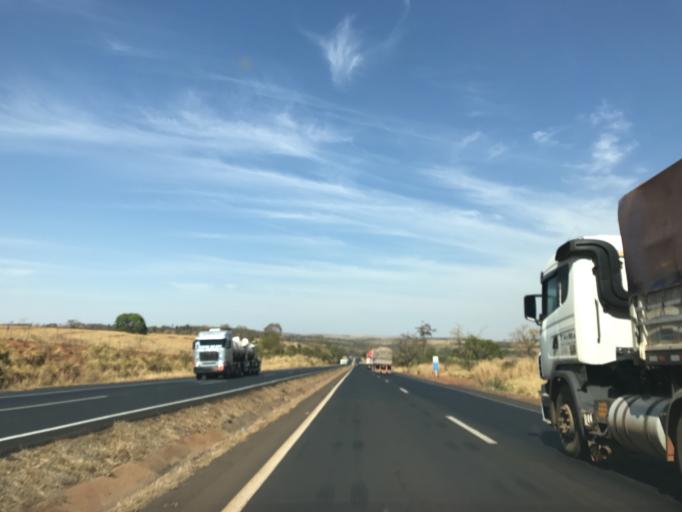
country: BR
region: Minas Gerais
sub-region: Monte Alegre De Minas
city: Monte Alegre de Minas
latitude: -18.7776
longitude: -49.0766
